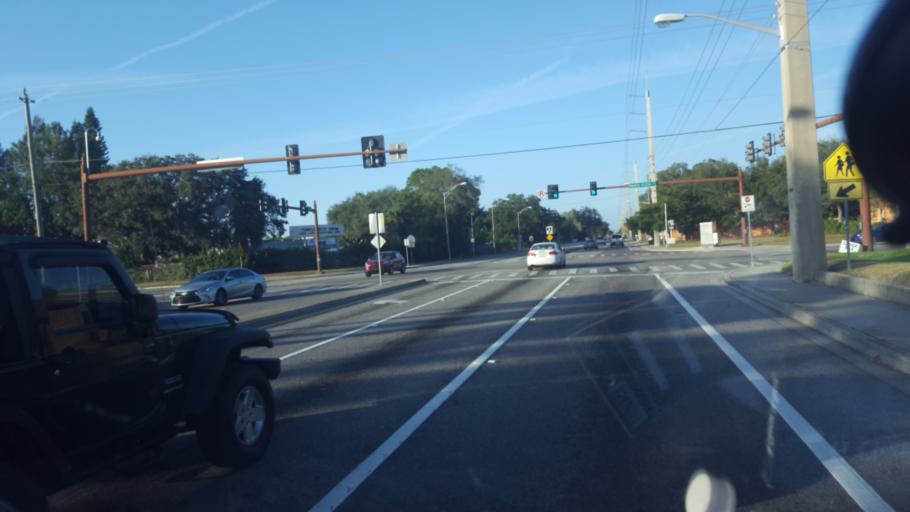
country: US
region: Florida
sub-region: Sarasota County
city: Southgate
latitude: 27.3224
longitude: -82.5140
